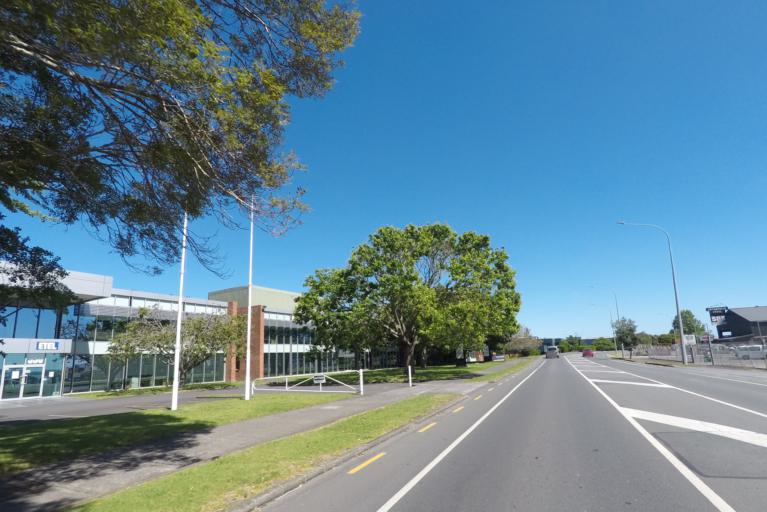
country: NZ
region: Auckland
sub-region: Auckland
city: Rosebank
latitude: -36.8785
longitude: 174.6707
